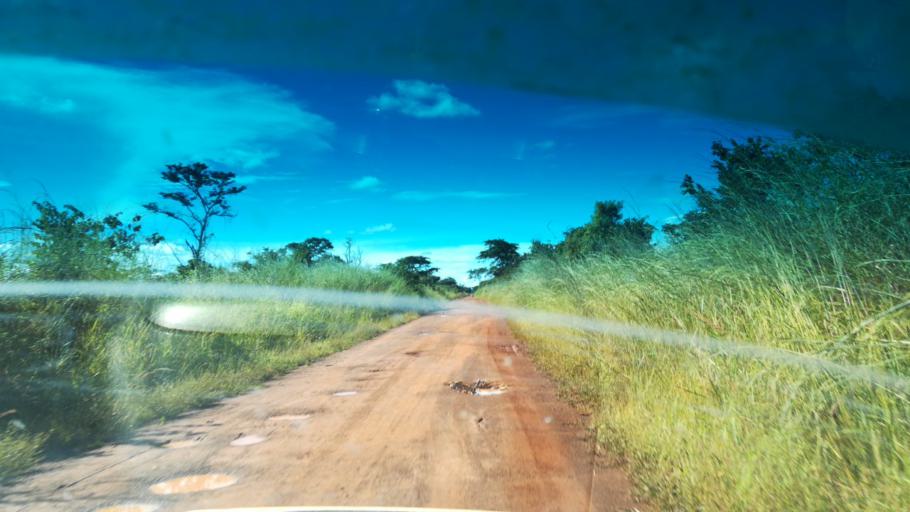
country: ZM
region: Luapula
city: Nchelenge
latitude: -9.4060
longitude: 28.1983
